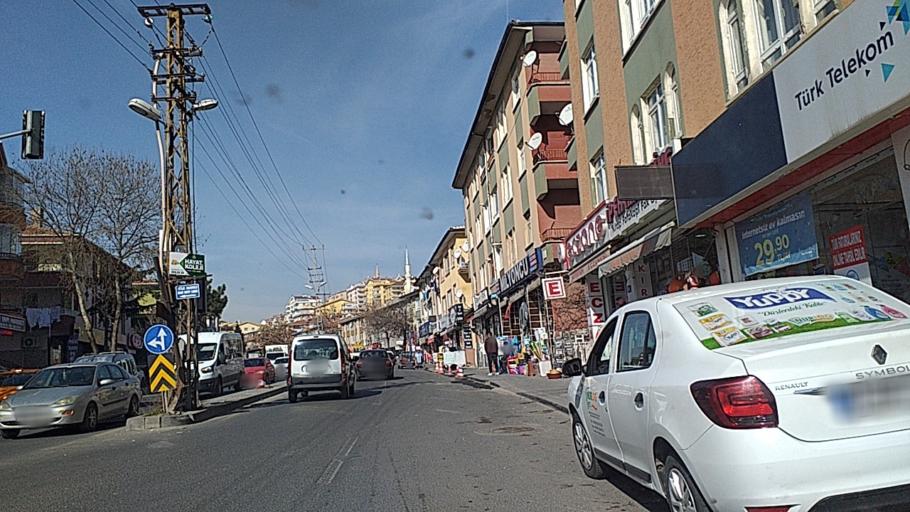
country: TR
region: Ankara
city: Ankara
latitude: 39.9843
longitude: 32.8313
